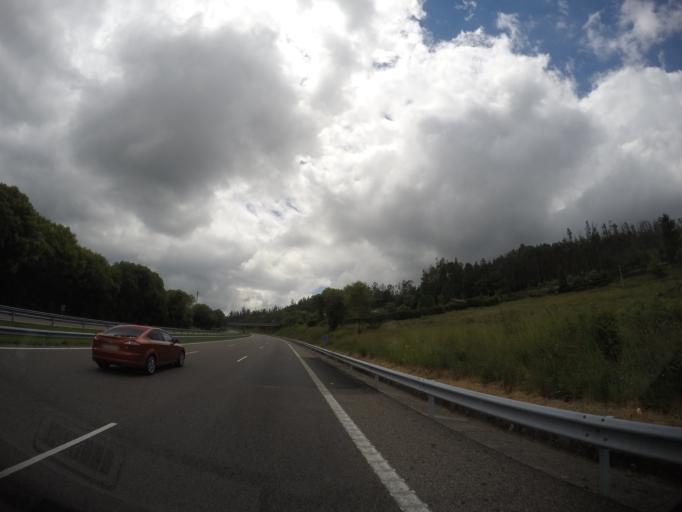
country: ES
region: Galicia
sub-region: Provincia da Coruna
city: Abegondo
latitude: 43.1918
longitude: -8.3096
